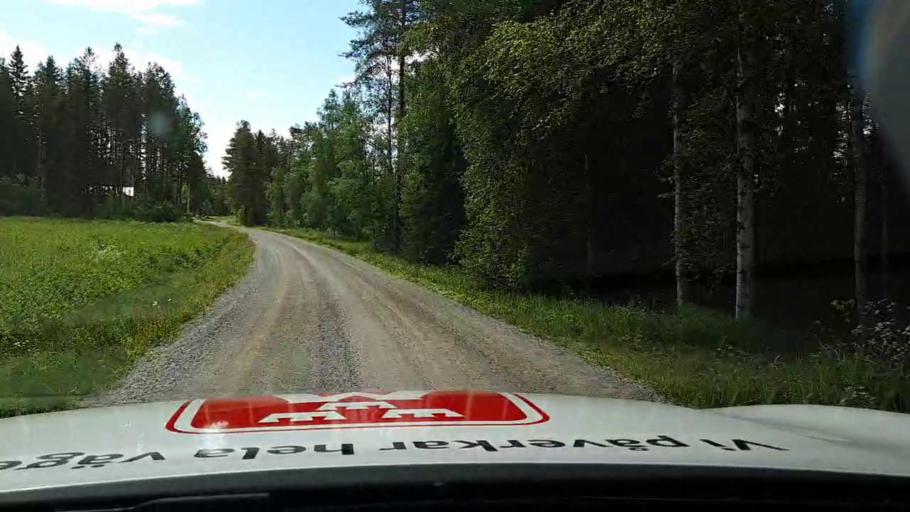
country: SE
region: Jaemtland
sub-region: Braecke Kommun
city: Braecke
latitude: 62.7513
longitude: 15.5023
